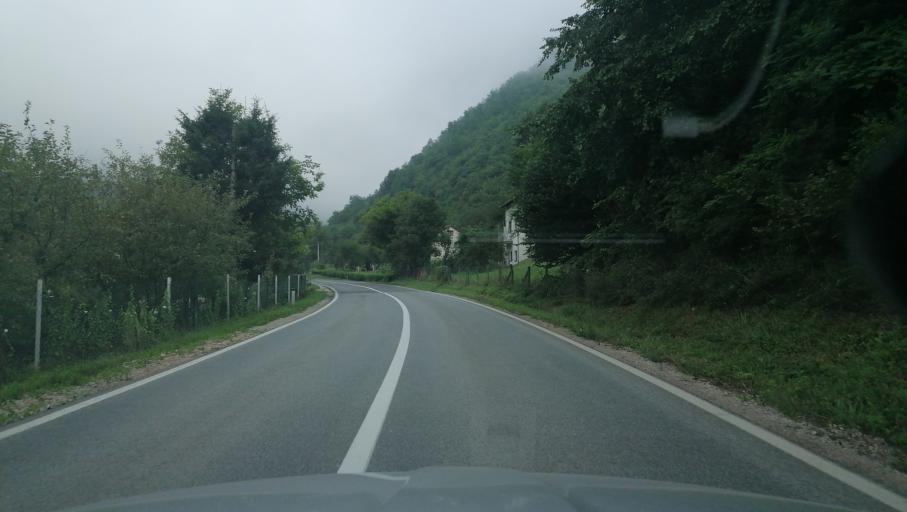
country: BA
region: Federation of Bosnia and Herzegovina
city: Donji Vakuf
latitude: 44.1596
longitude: 17.3685
